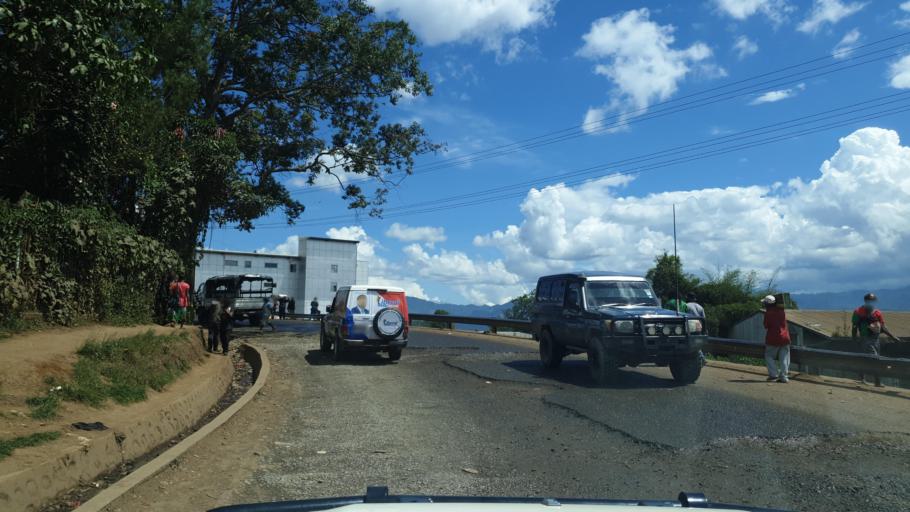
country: PG
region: Eastern Highlands
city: Goroka
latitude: -6.0722
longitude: 145.3890
